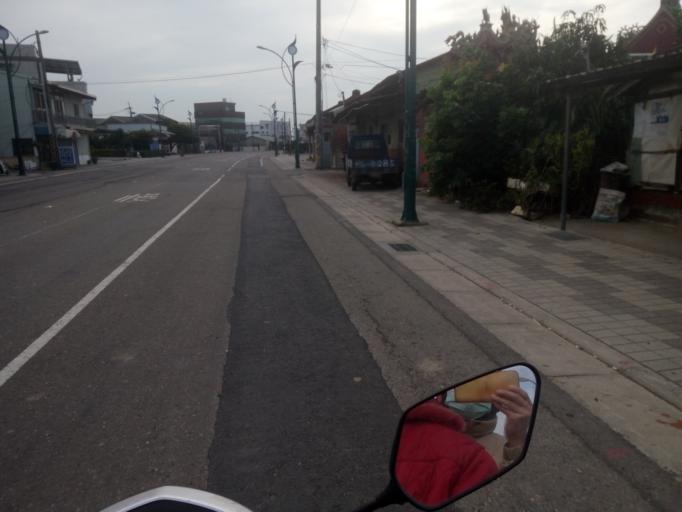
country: TW
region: Taiwan
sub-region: Chiayi
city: Taibao
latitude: 23.4917
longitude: 120.3540
